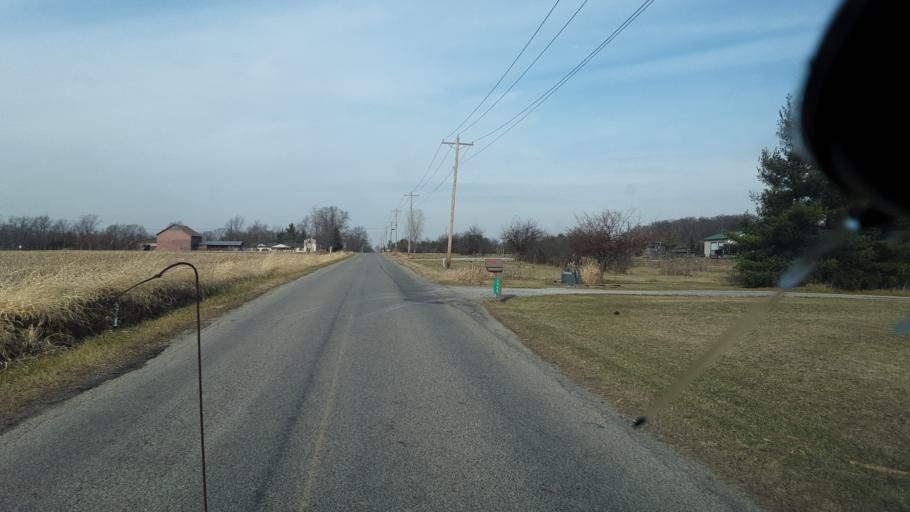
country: US
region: Indiana
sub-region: DeKalb County
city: Butler
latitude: 41.3894
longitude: -84.8890
